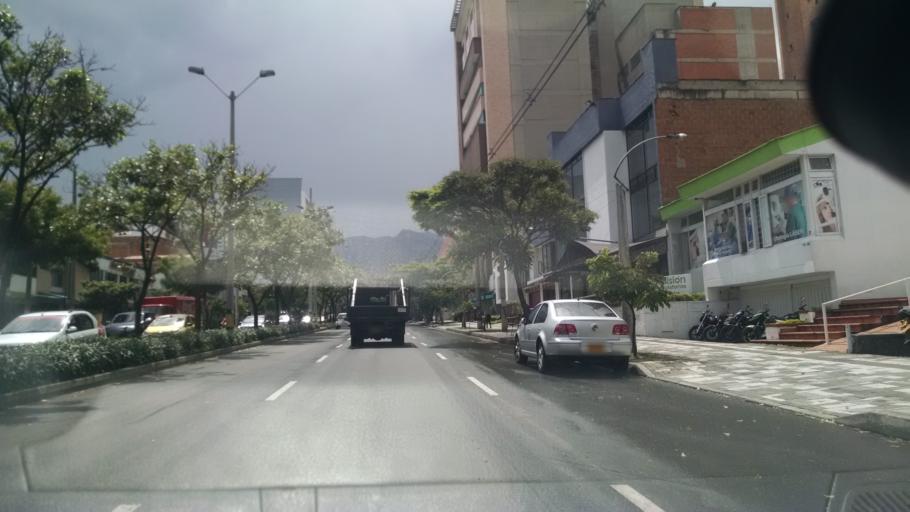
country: CO
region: Antioquia
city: Medellin
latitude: 6.2390
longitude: -75.5986
